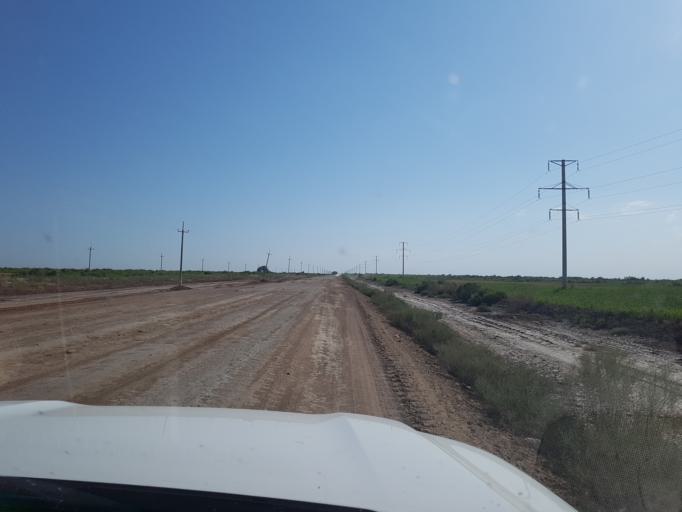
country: TM
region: Dasoguz
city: Koeneuergench
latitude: 42.1176
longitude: 58.9275
